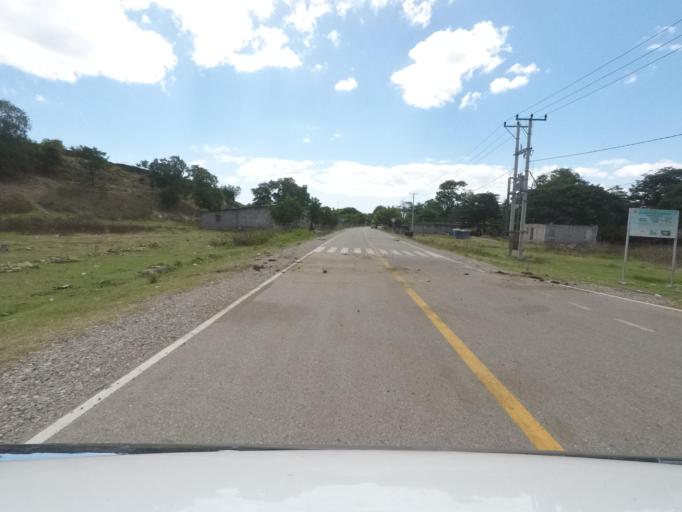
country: TL
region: Lautem
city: Lospalos
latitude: -8.4018
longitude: 126.8309
